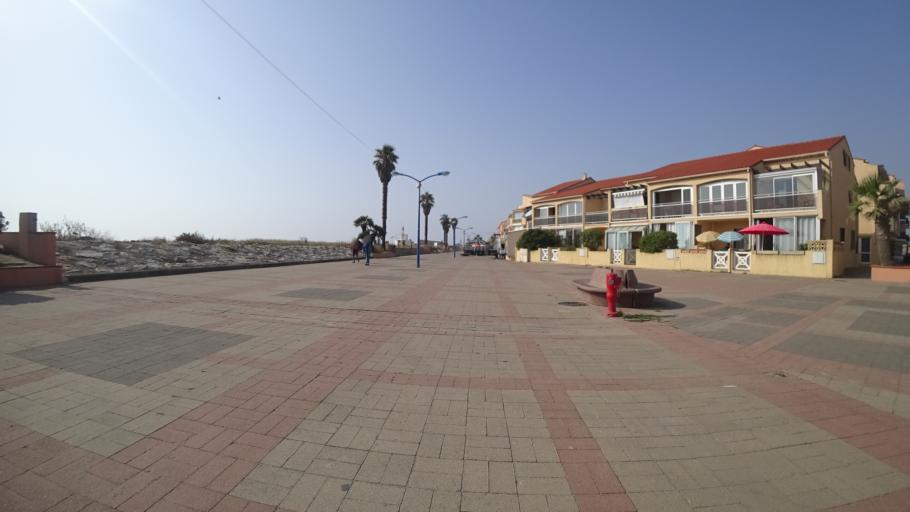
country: FR
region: Languedoc-Roussillon
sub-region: Departement des Pyrenees-Orientales
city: Sainte-Marie-Plage
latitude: 42.7354
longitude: 3.0369
